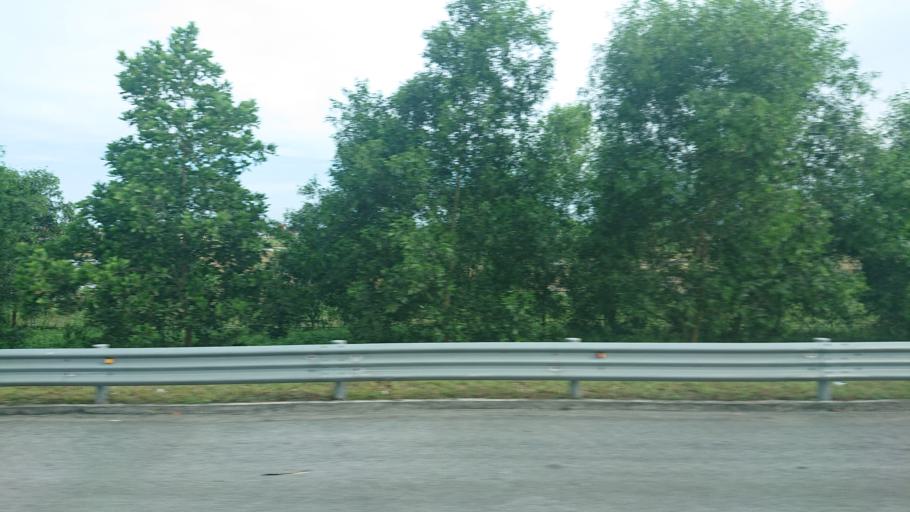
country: VN
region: Hai Phong
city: Nui Doi
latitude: 20.7657
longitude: 106.6517
